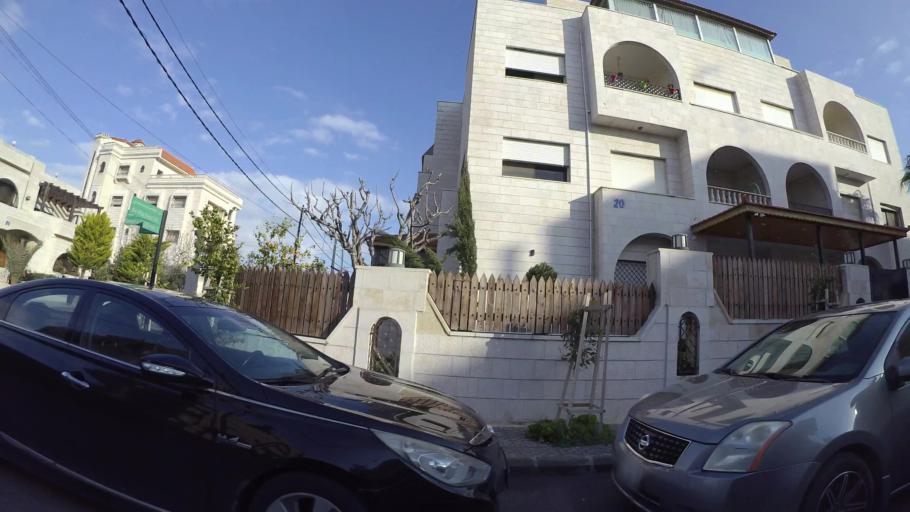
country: JO
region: Amman
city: Al Jubayhah
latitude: 31.9840
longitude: 35.8700
